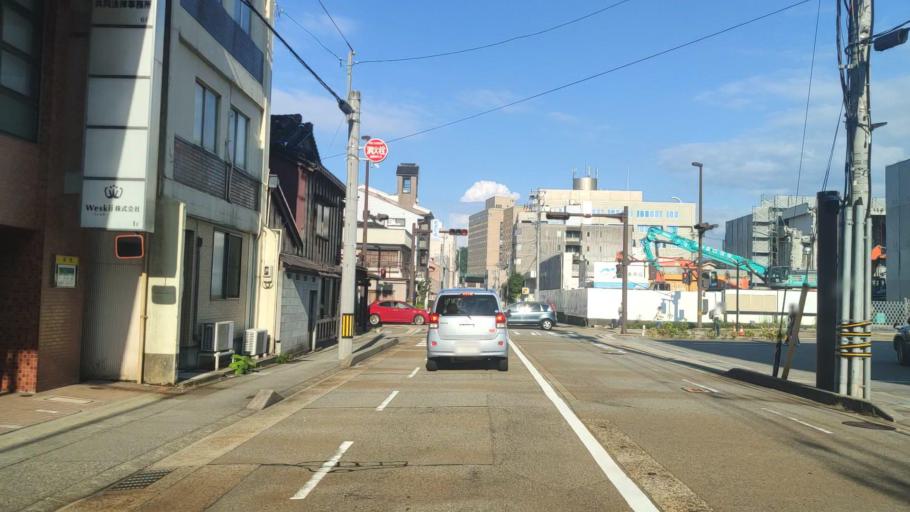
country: JP
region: Ishikawa
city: Kanazawa-shi
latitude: 36.5700
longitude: 136.6609
